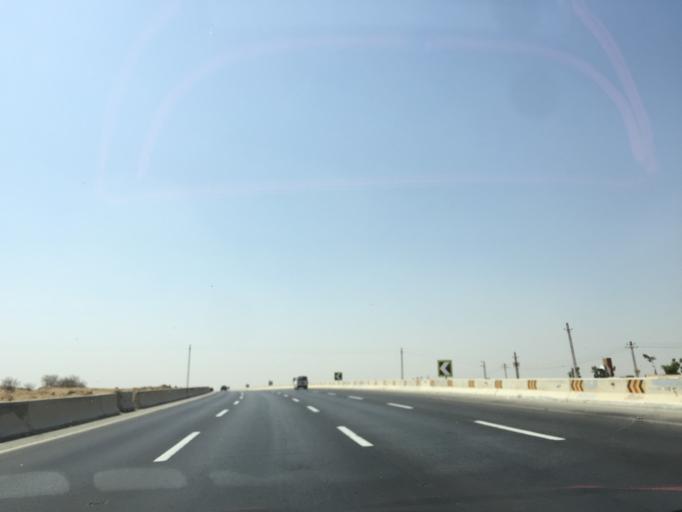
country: EG
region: Al Jizah
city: Awsim
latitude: 30.0889
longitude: 30.9719
